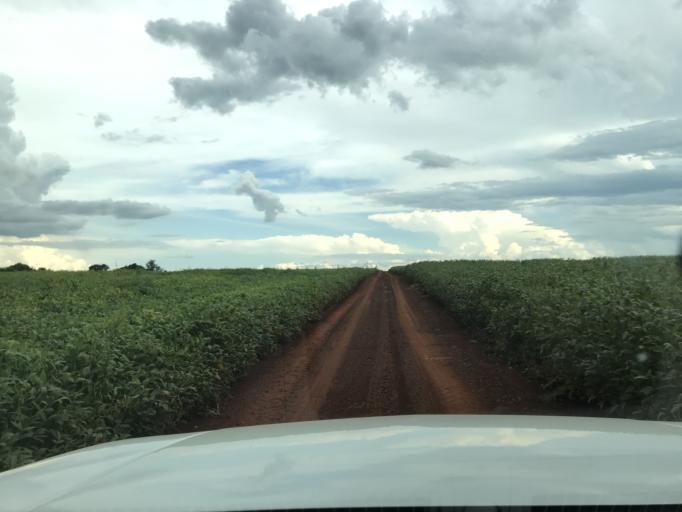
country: BR
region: Parana
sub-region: Palotina
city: Palotina
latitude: -24.2704
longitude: -53.7686
